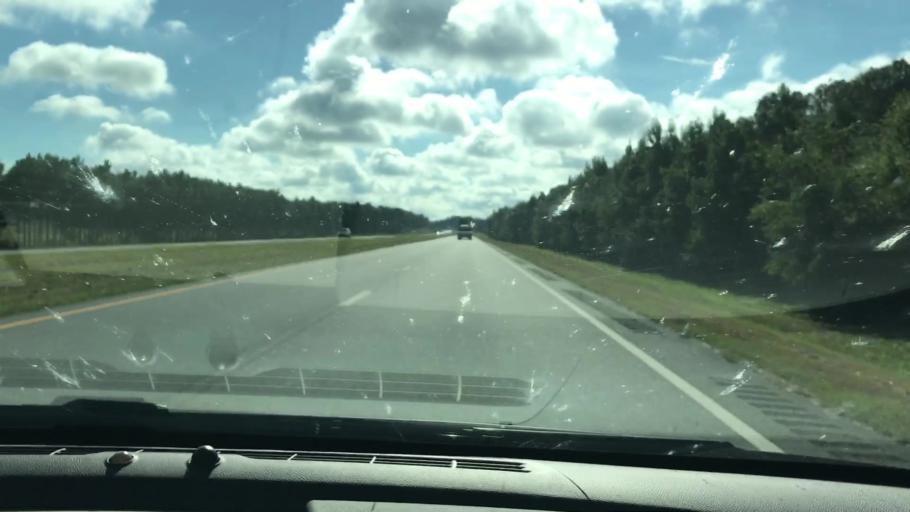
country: US
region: Georgia
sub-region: Worth County
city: Sylvester
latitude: 31.5527
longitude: -83.9795
